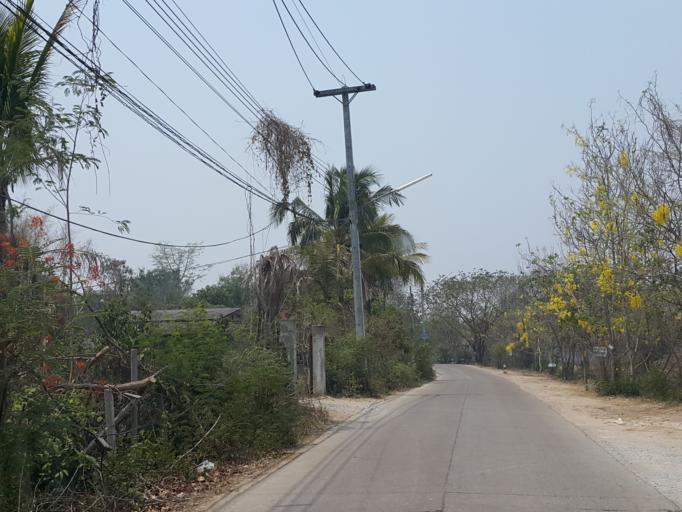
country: TH
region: Chiang Mai
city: Chiang Mai
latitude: 18.7524
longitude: 98.9753
